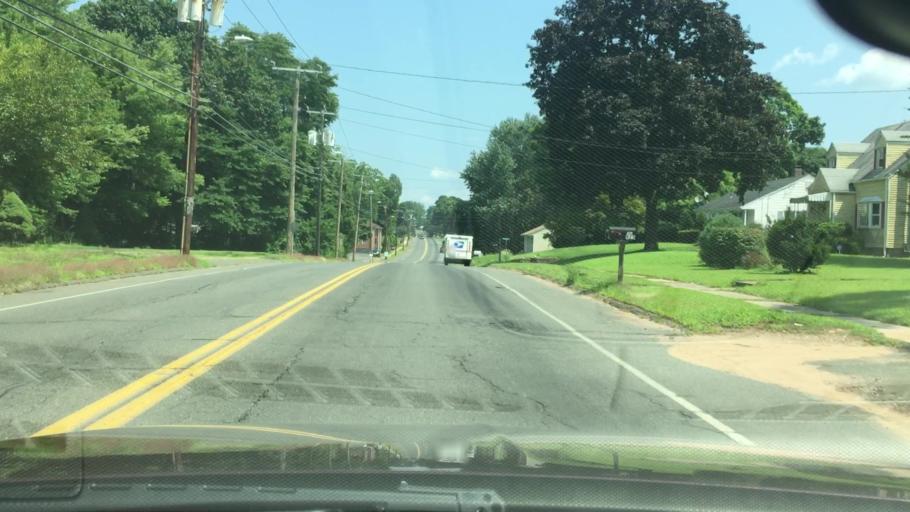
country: US
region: Connecticut
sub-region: Hartford County
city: East Hartford
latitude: 41.7871
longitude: -72.5914
